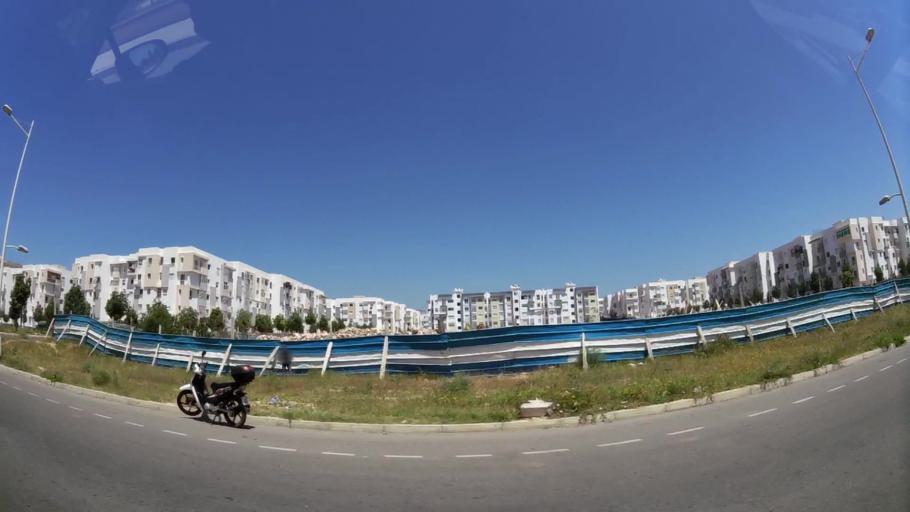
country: MA
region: Oued ed Dahab-Lagouira
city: Dakhla
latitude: 30.4364
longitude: -9.5602
